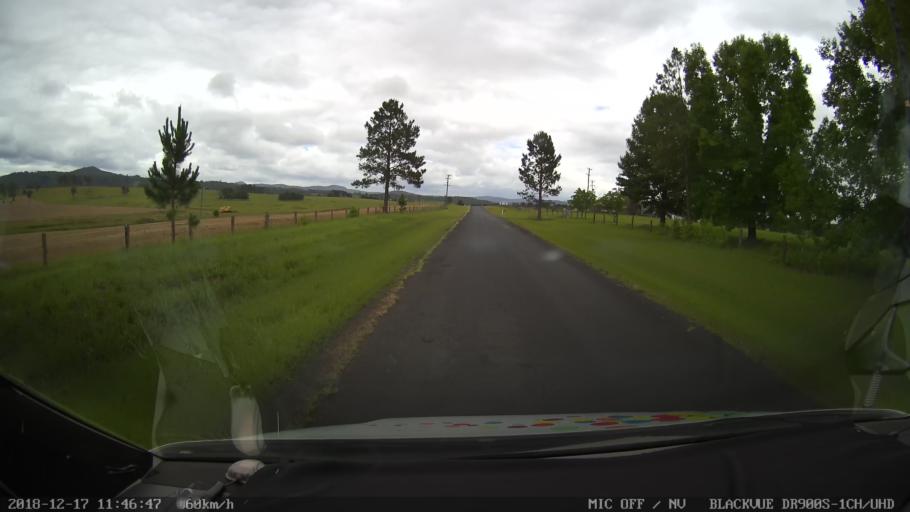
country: AU
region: New South Wales
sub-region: Kyogle
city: Kyogle
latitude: -28.6336
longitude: 152.5925
